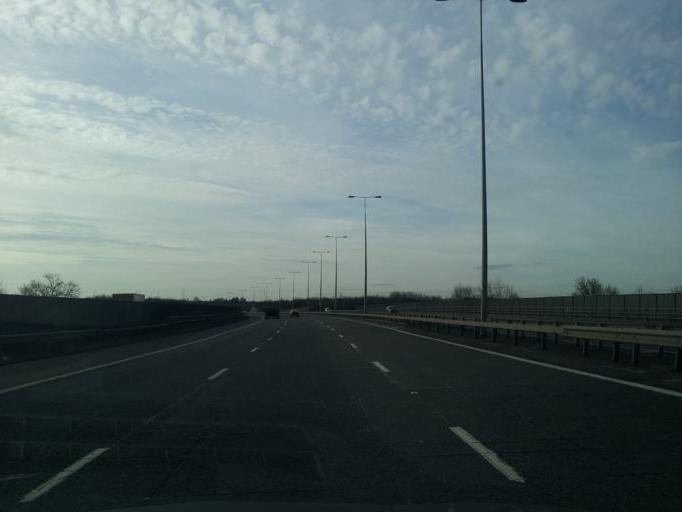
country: GB
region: England
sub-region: Cambridgeshire
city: Great Stukeley
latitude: 52.3657
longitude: -0.2547
